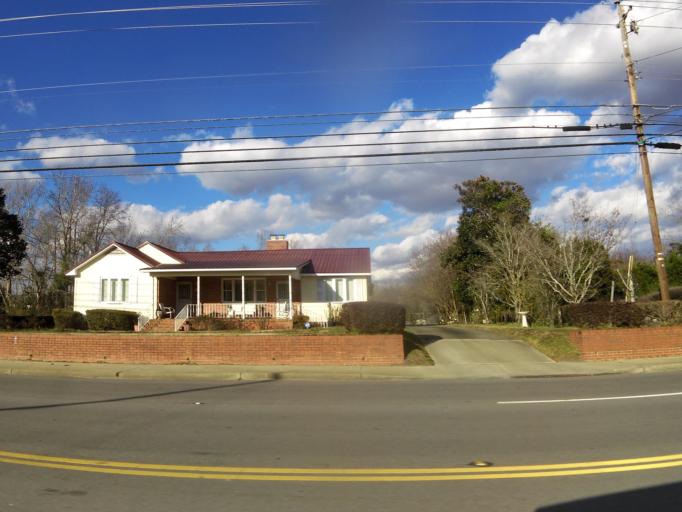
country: US
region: South Carolina
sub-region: Clarendon County
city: Manning
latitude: 33.6964
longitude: -80.2209
